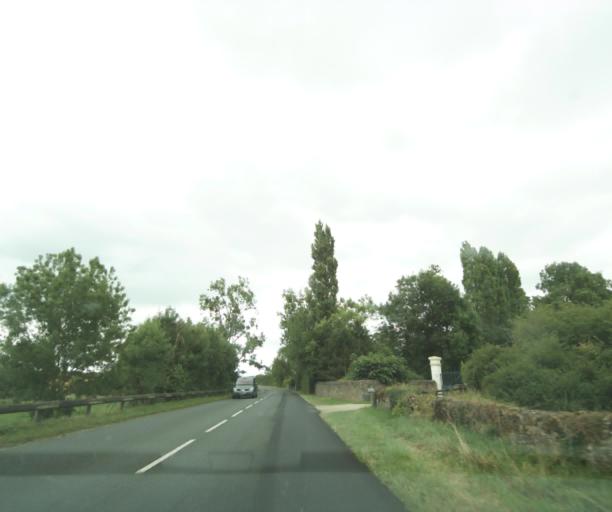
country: FR
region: Pays de la Loire
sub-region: Departement de la Sarthe
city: Precigne
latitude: 47.7855
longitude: -0.3180
